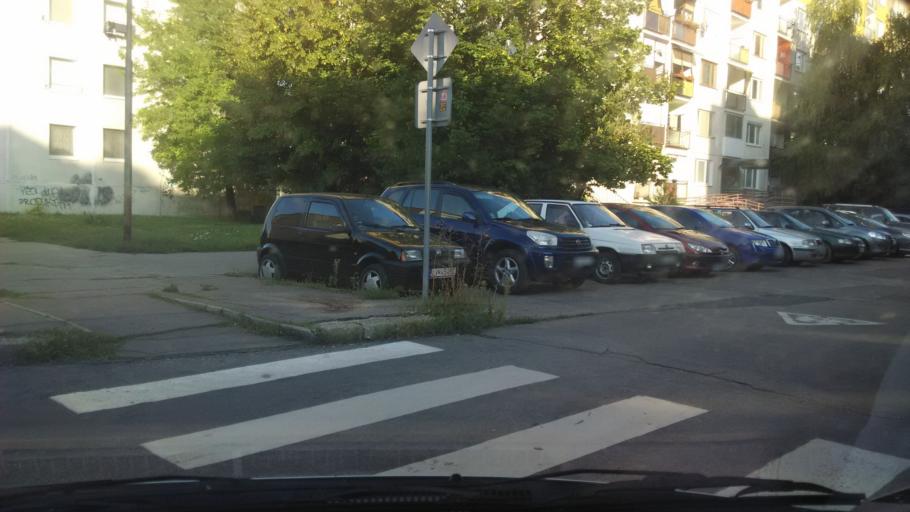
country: SK
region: Nitriansky
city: Levice
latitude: 48.2165
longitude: 18.6251
